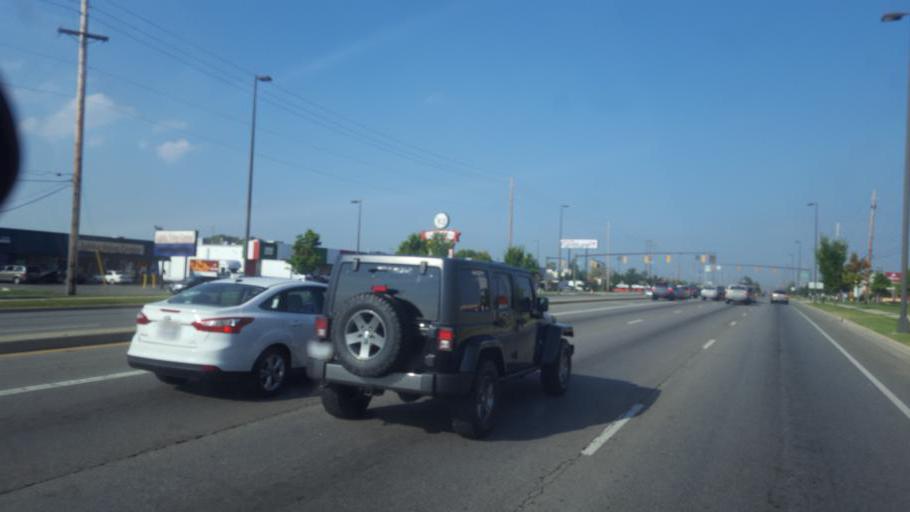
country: US
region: Ohio
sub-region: Franklin County
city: Minerva Park
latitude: 40.0600
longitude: -82.9603
